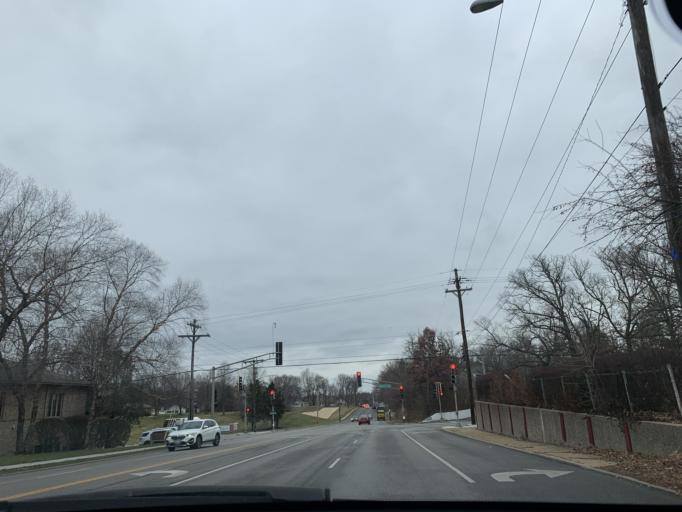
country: US
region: Illinois
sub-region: Sangamon County
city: Leland Grove
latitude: 39.7935
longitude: -89.6869
